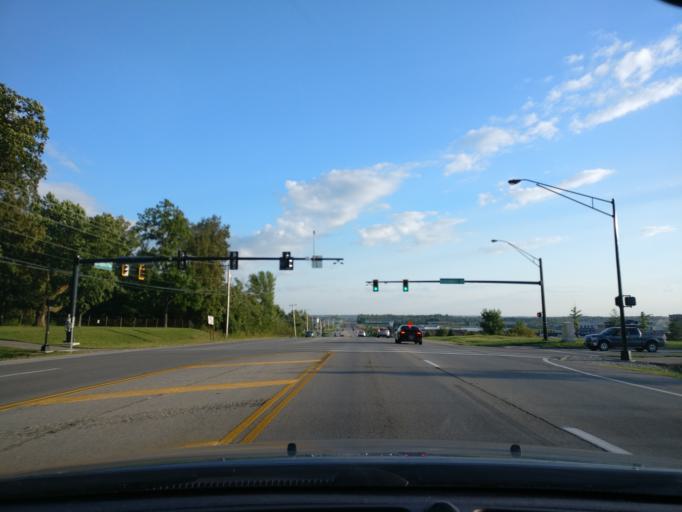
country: US
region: Ohio
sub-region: Warren County
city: Five Points
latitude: 39.6040
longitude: -84.2286
